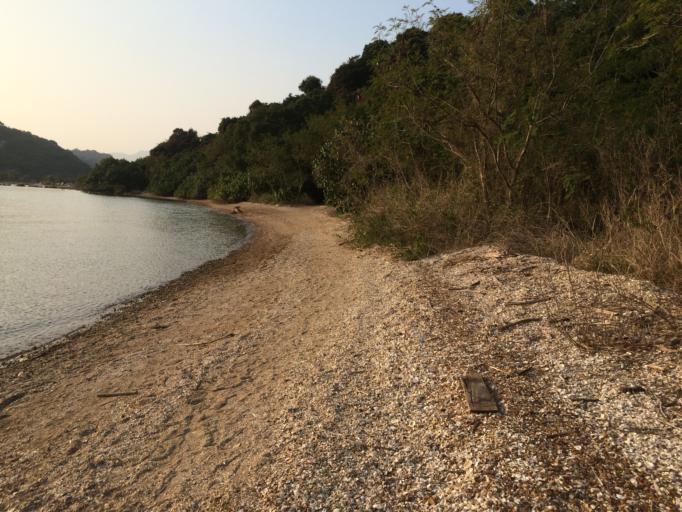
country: HK
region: Tai Po
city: Tai Po
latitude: 22.4497
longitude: 114.2247
